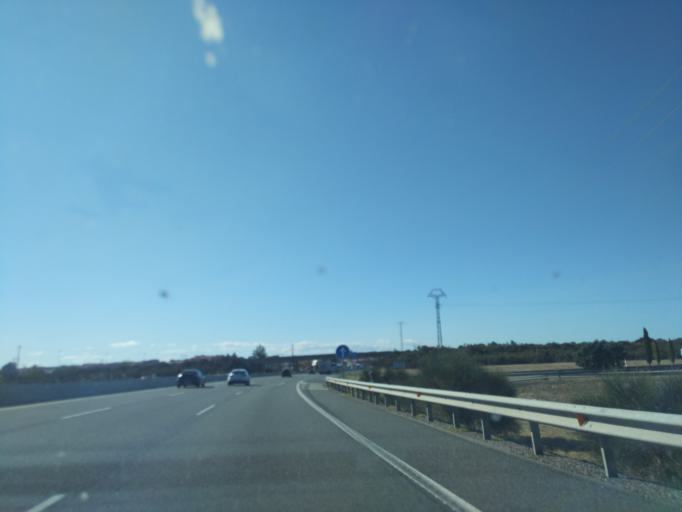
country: ES
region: Castille and Leon
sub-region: Provincia de Zamora
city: Villanueva de Azoague
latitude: 41.9981
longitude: -5.6542
